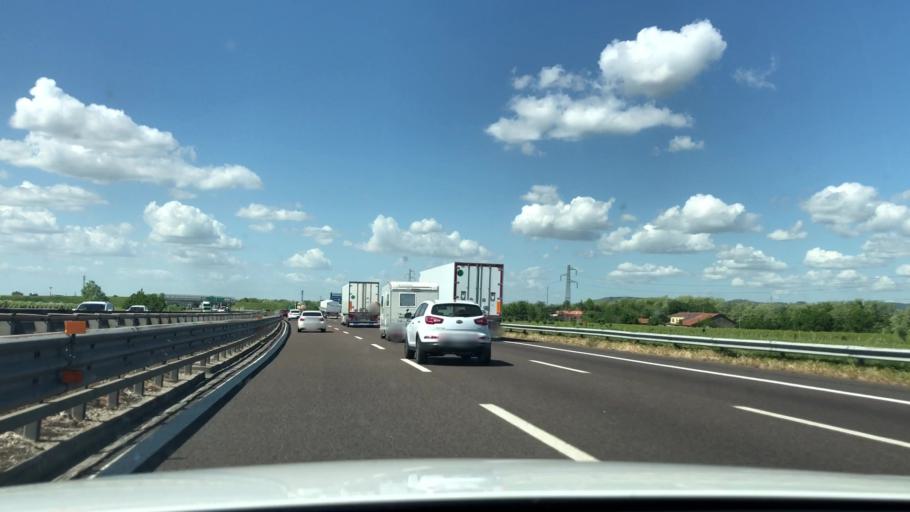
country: IT
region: Veneto
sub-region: Provincia di Vicenza
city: Montebello Vicentino
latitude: 45.4407
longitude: 11.3666
